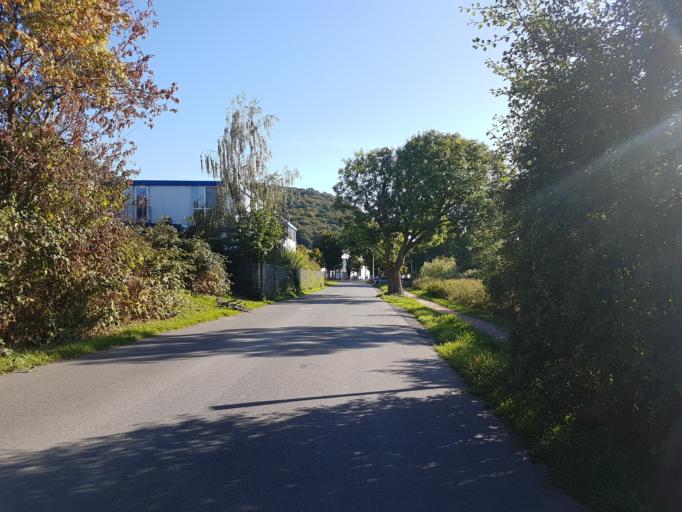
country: DE
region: North Rhine-Westphalia
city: Porta Westfalica
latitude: 52.2522
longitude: 8.9231
